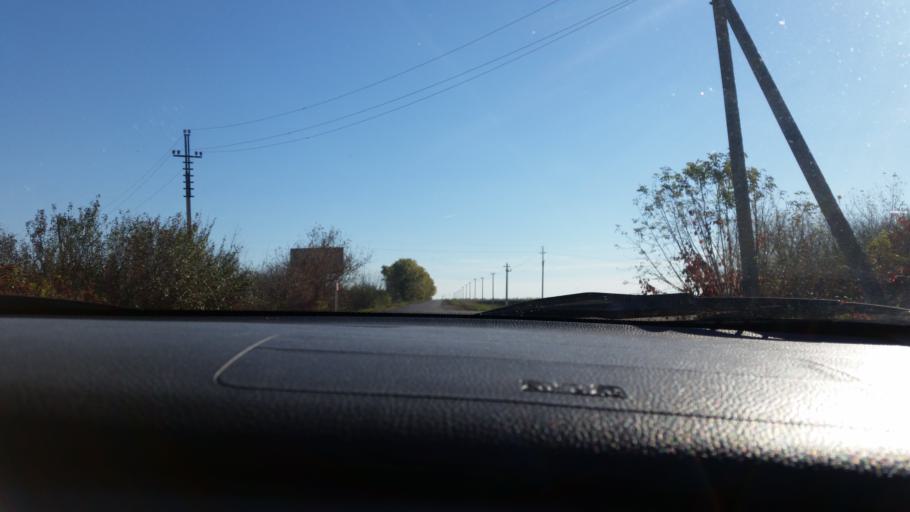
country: RU
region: Lipetsk
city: Gryazi
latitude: 52.4603
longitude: 39.9596
